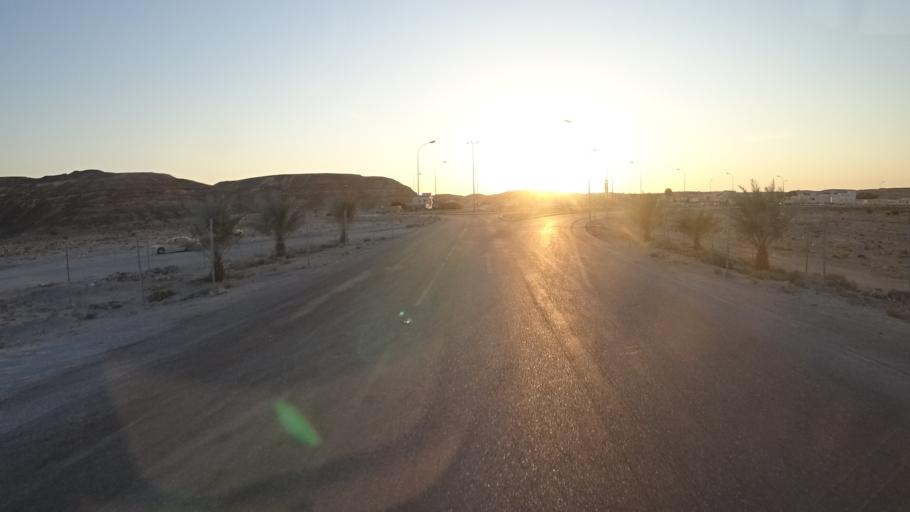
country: OM
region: Zufar
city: Salalah
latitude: 17.4887
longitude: 53.3548
